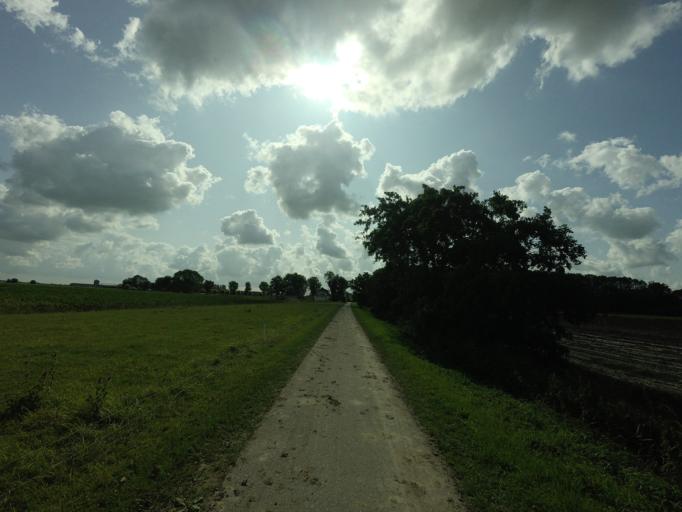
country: NL
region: Friesland
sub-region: Gemeente Het Bildt
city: Minnertsga
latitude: 53.2592
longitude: 5.5966
